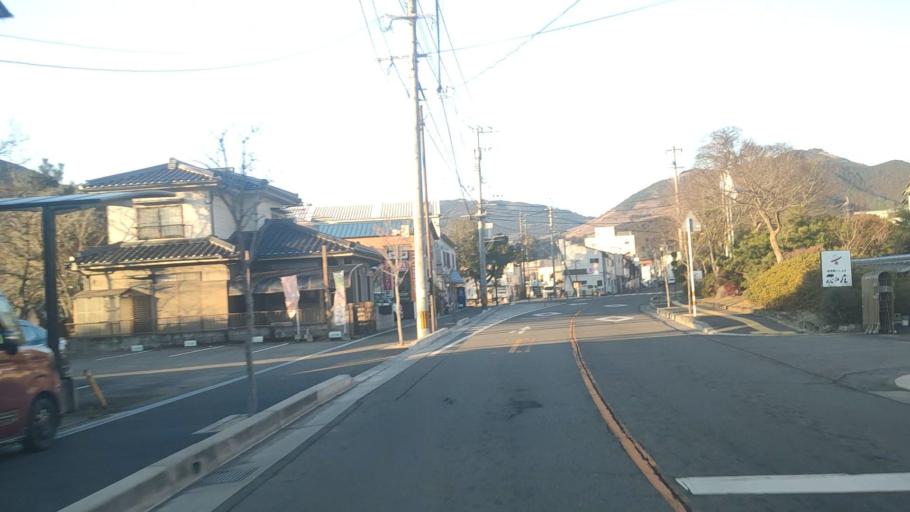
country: JP
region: Oita
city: Beppu
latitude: 33.2601
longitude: 131.3561
